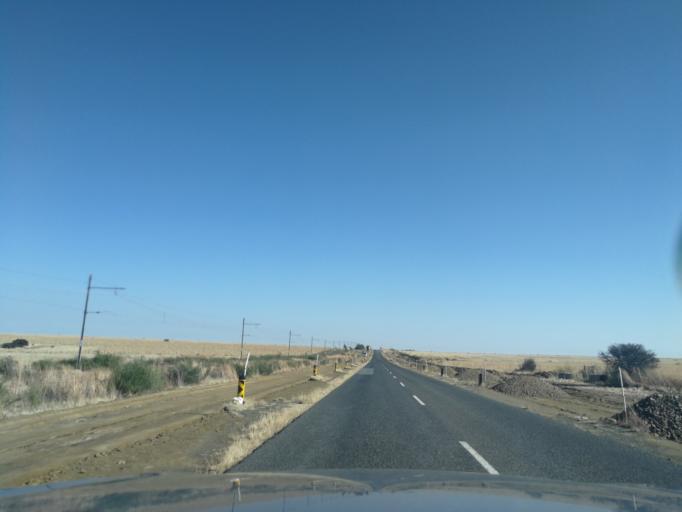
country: ZA
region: Orange Free State
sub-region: Fezile Dabi District Municipality
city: Kroonstad
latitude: -27.8960
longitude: 27.4970
